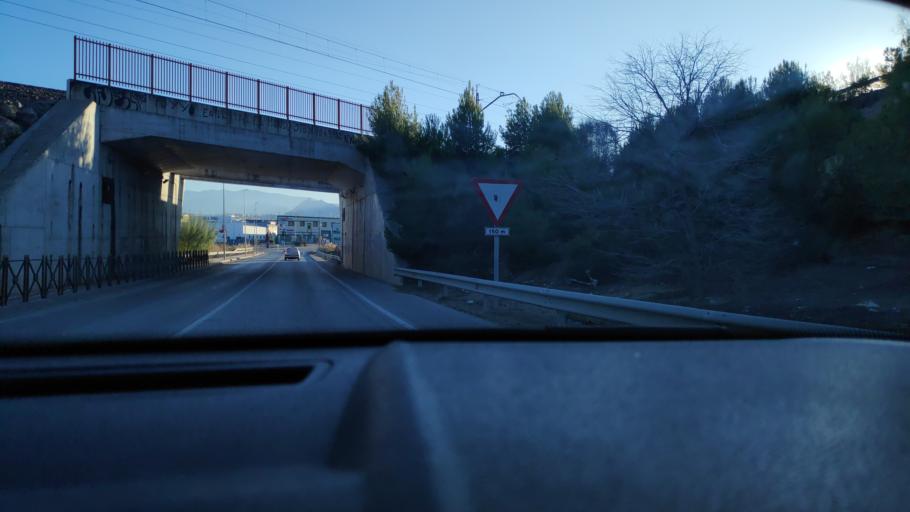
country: ES
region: Andalusia
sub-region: Provincia de Jaen
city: Jaen
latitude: 37.8041
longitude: -3.7881
